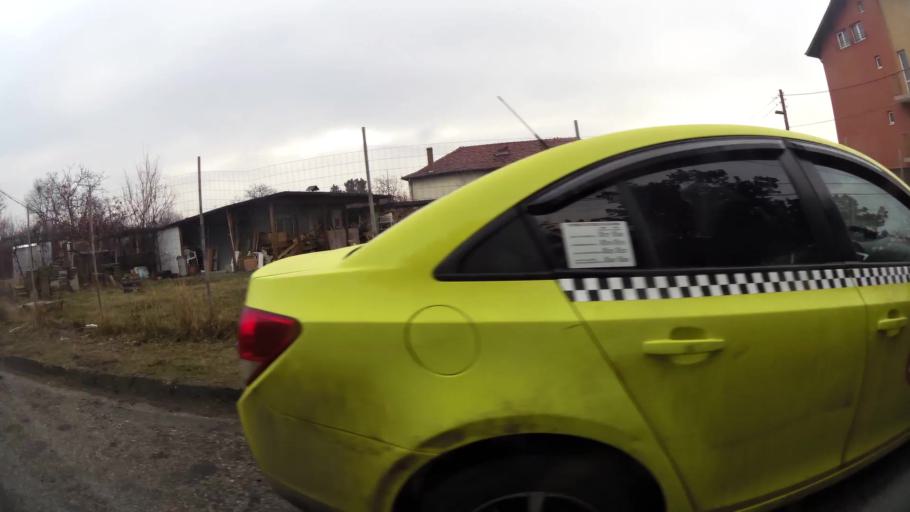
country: BG
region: Sofia-Capital
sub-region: Stolichna Obshtina
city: Sofia
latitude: 42.7451
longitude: 23.3471
